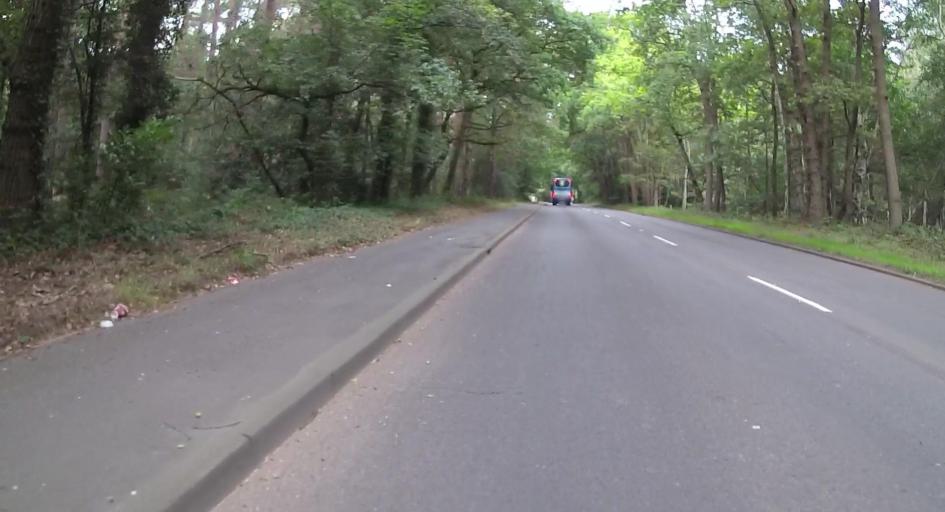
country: GB
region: England
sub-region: Surrey
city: Woking
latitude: 51.3301
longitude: -0.5444
